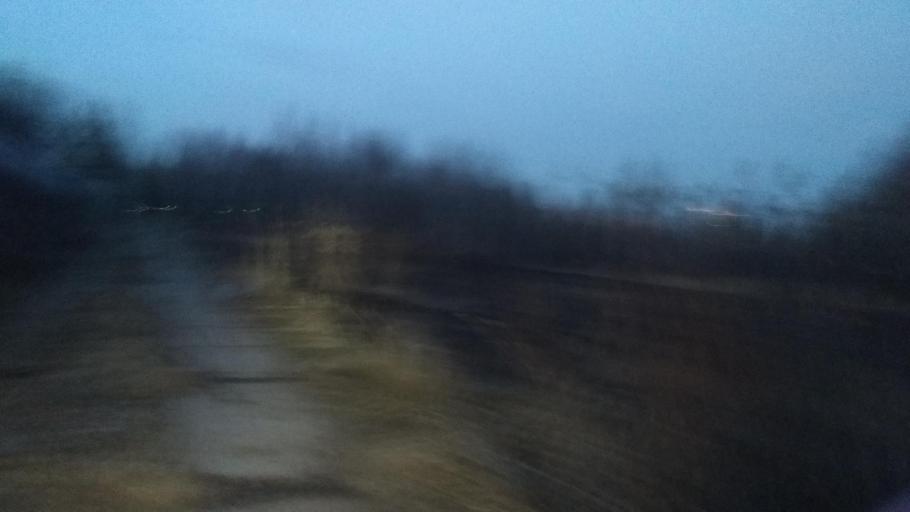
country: RU
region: Moscow
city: Orekhovo-Borisovo
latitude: 55.5938
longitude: 37.7076
